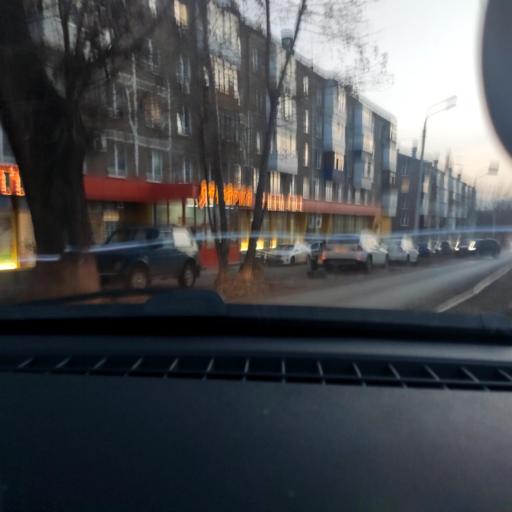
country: RU
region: Bashkortostan
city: Ufa
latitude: 54.8148
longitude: 56.0782
